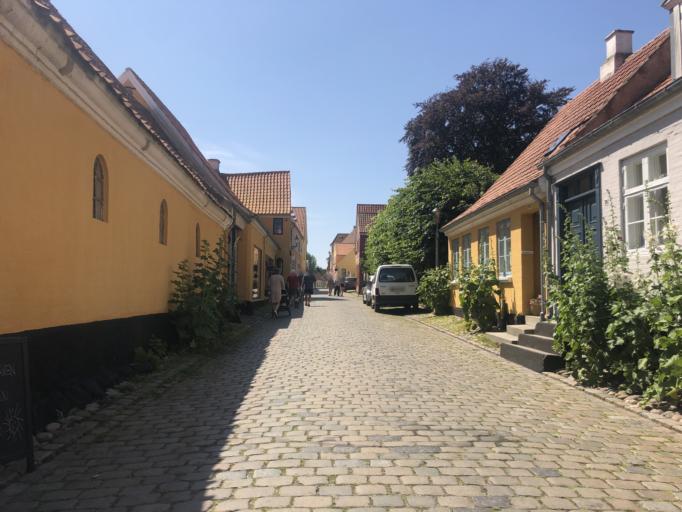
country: DK
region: South Denmark
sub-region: AEro Kommune
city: AEroskobing
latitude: 54.8890
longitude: 10.4098
